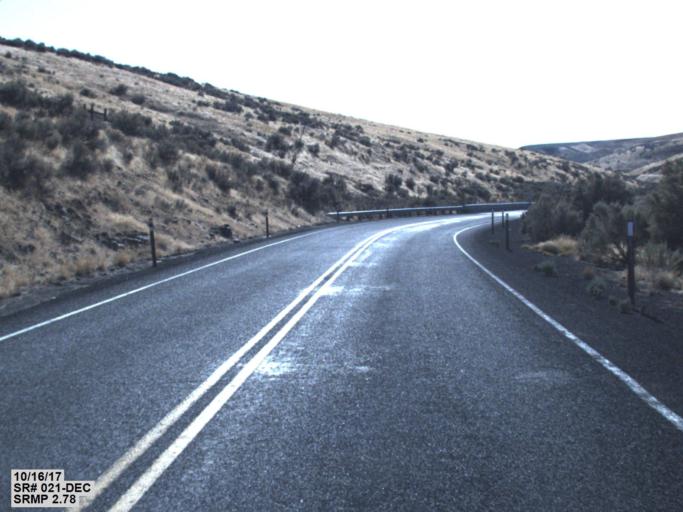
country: US
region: Washington
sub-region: Franklin County
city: Connell
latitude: 46.6793
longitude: -118.5385
